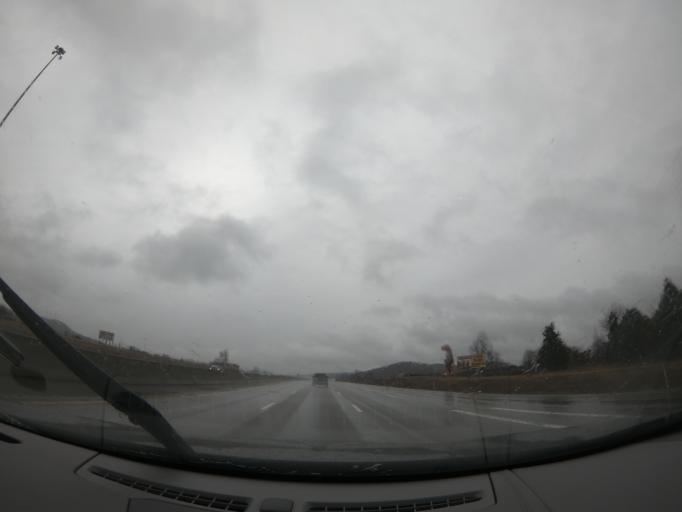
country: US
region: Kentucky
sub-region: Barren County
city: Cave City
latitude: 37.1329
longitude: -85.9813
